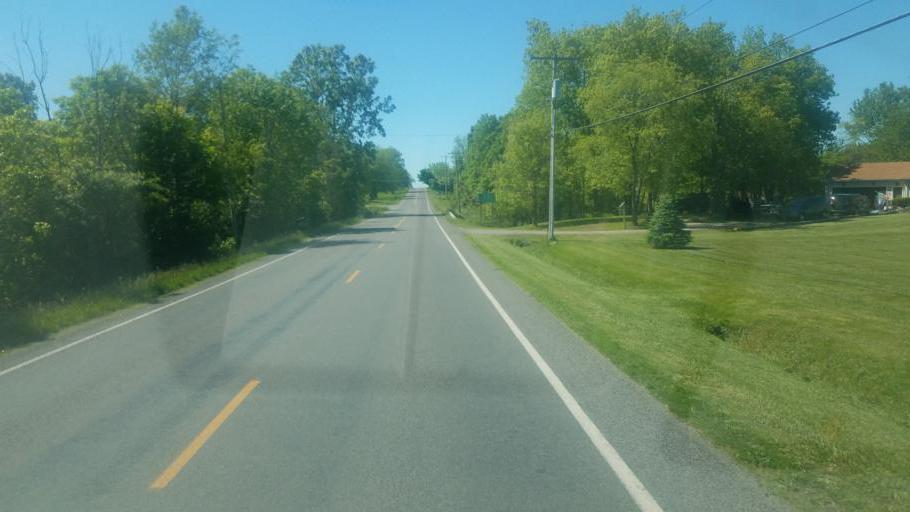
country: US
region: Ohio
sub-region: Logan County
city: Bellefontaine
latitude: 40.3839
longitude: -83.7843
